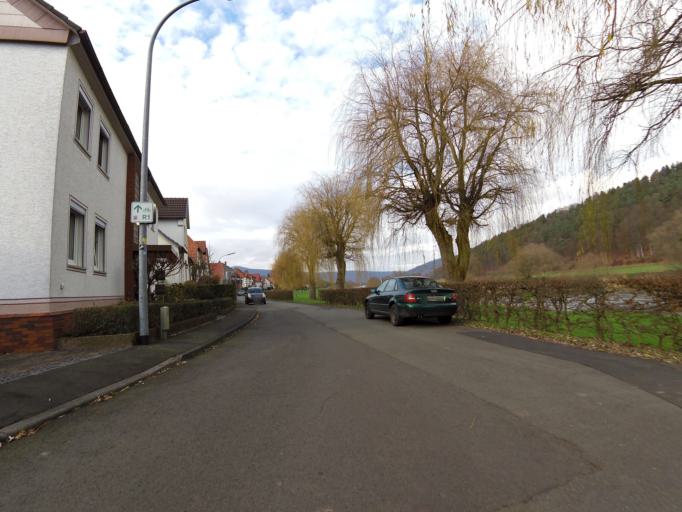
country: DE
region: Lower Saxony
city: Buhren
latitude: 51.4791
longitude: 9.6209
